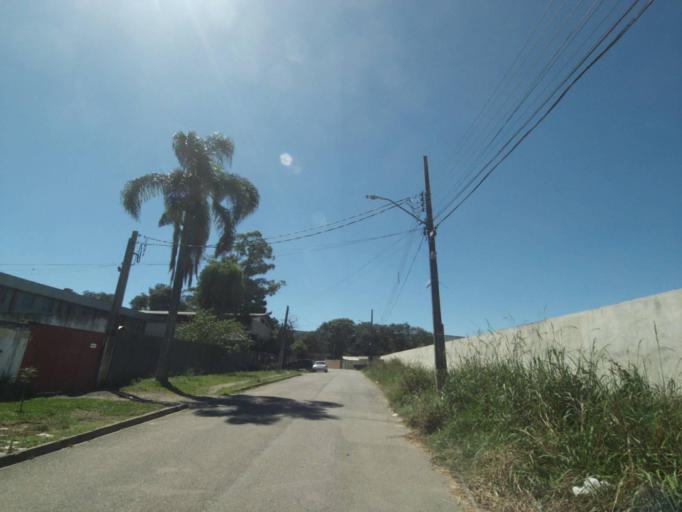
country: BR
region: Parana
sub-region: Curitiba
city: Curitiba
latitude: -25.4701
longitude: -49.3512
